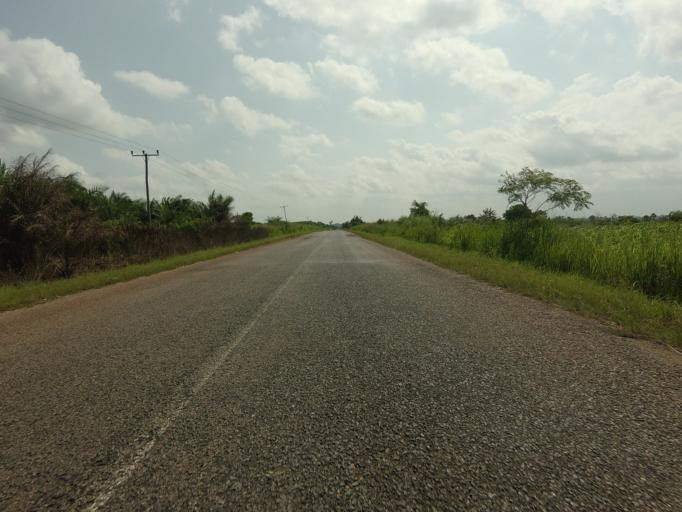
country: TG
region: Maritime
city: Tsevie
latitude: 6.3923
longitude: 0.8245
